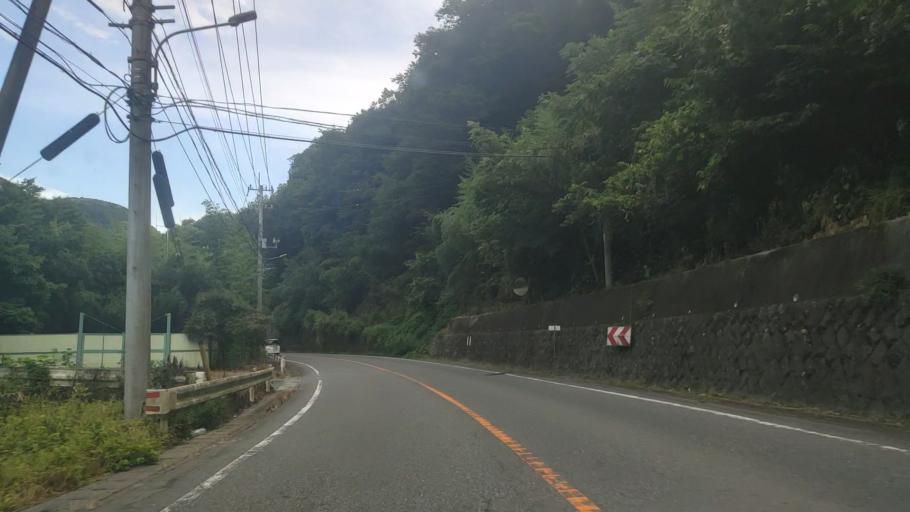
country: JP
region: Gunma
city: Omamacho-omama
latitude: 36.4878
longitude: 139.2645
